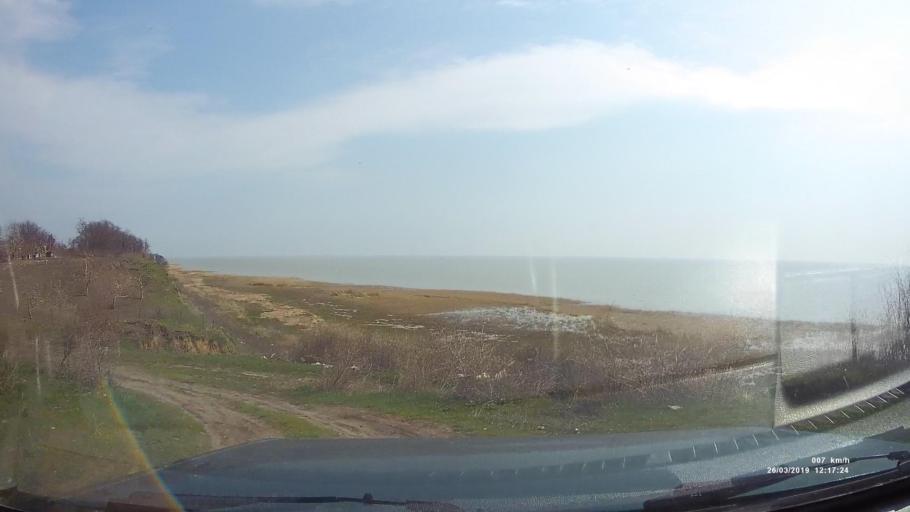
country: RU
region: Rostov
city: Novobessergenovka
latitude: 47.1452
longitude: 38.6424
